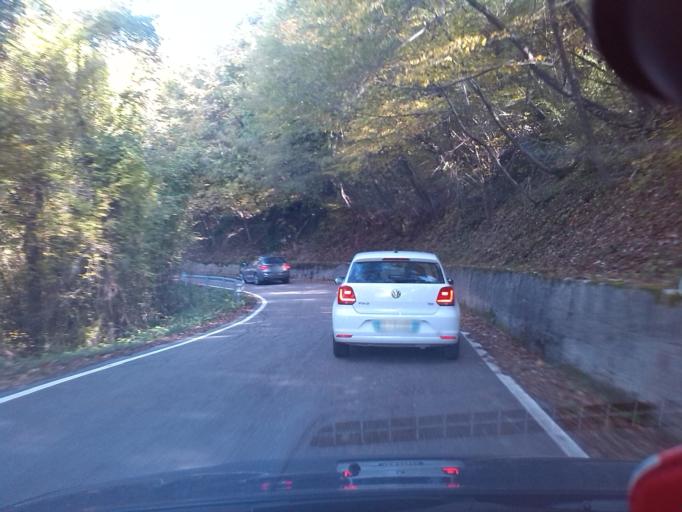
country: IT
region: Friuli Venezia Giulia
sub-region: Provincia di Udine
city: San Leonardo
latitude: 46.0998
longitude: 13.5310
